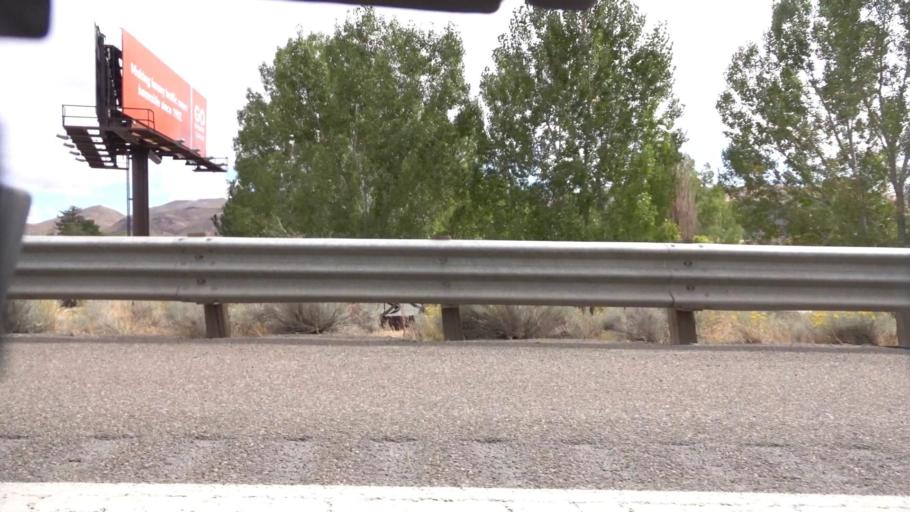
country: US
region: Nevada
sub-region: Elko County
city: Elko
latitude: 40.8880
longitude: -115.7134
